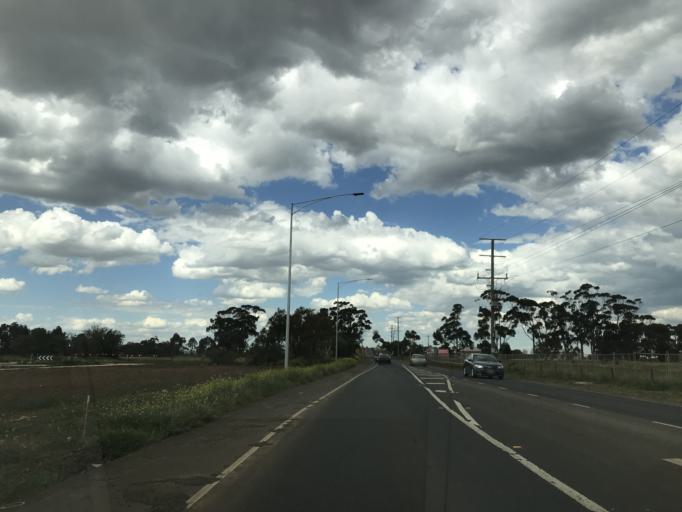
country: AU
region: Victoria
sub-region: Wyndham
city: Truganina
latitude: -37.8224
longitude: 144.7181
